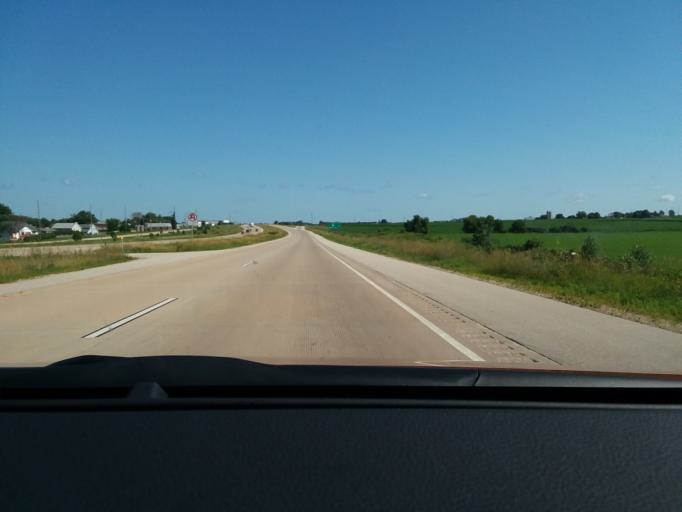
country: US
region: Wisconsin
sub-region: Dane County
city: De Forest
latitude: 43.2430
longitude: -89.3226
